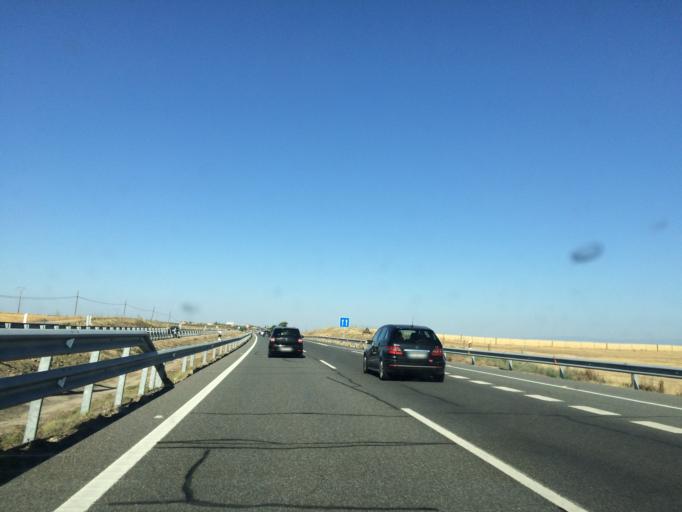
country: ES
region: Castille-La Mancha
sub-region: Province of Toledo
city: Herreruela de Oropesa
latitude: 39.9024
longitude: -5.2480
